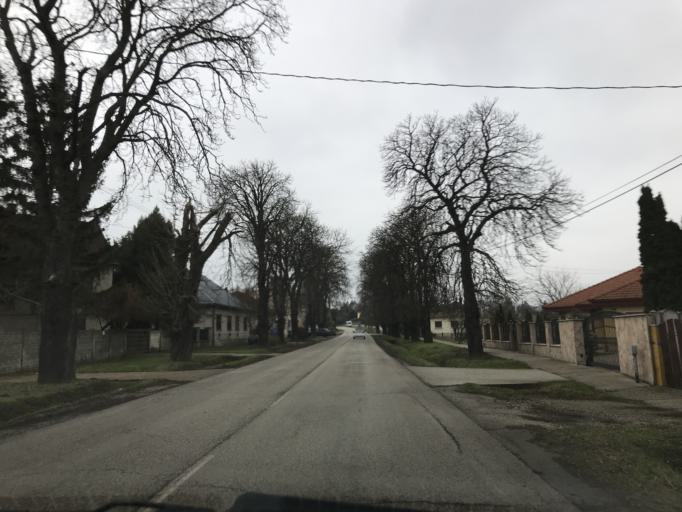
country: HU
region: Komarom-Esztergom
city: Tokod
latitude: 47.7276
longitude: 18.6680
